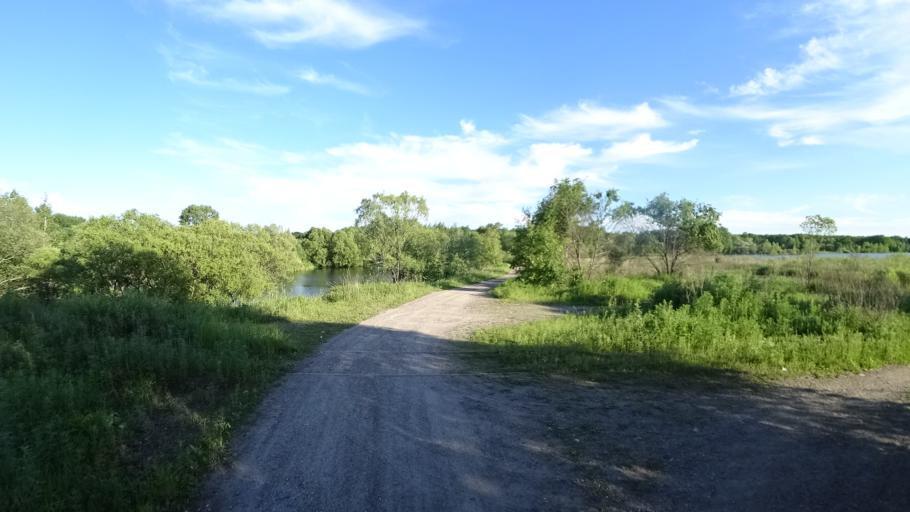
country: RU
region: Khabarovsk Krai
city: Khor
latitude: 47.8529
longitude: 134.9416
